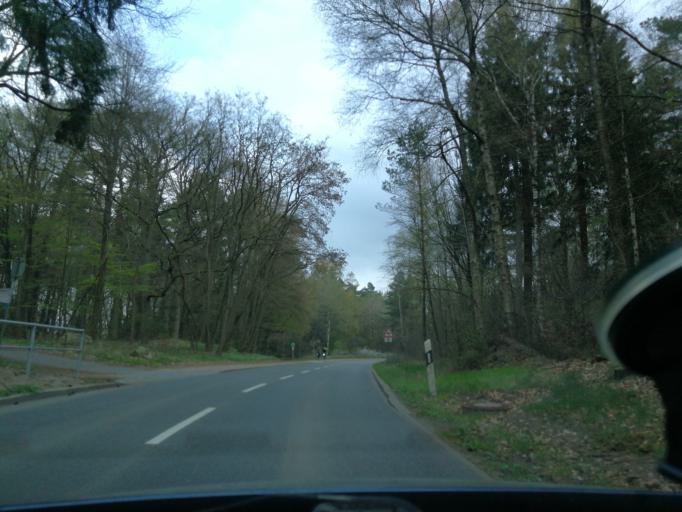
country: DE
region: Lower Saxony
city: Seevetal
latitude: 53.4464
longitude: 9.9174
